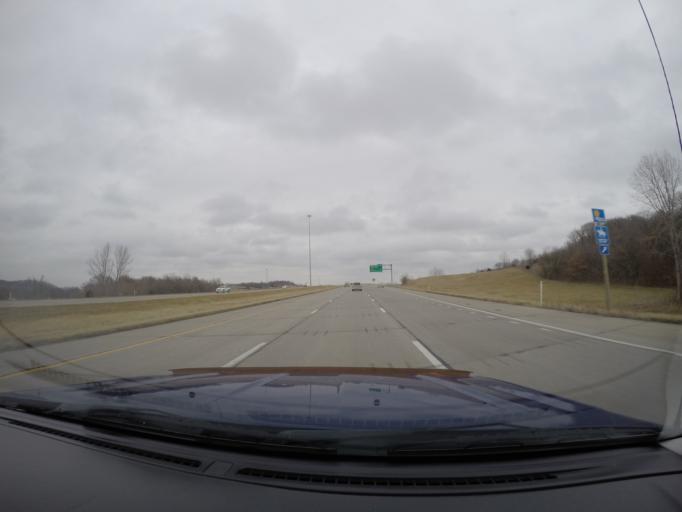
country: US
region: Kansas
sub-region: Wyandotte County
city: Edwardsville
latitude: 39.1766
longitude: -94.8028
